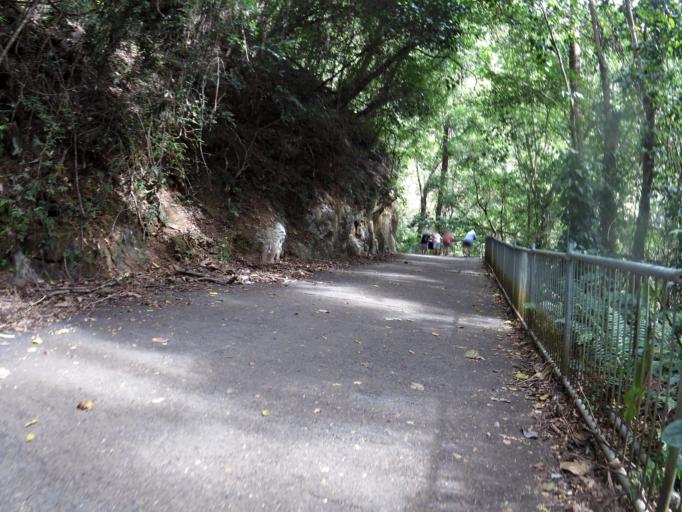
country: AU
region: Queensland
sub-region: Cairns
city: Woree
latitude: -16.9657
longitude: 145.6744
